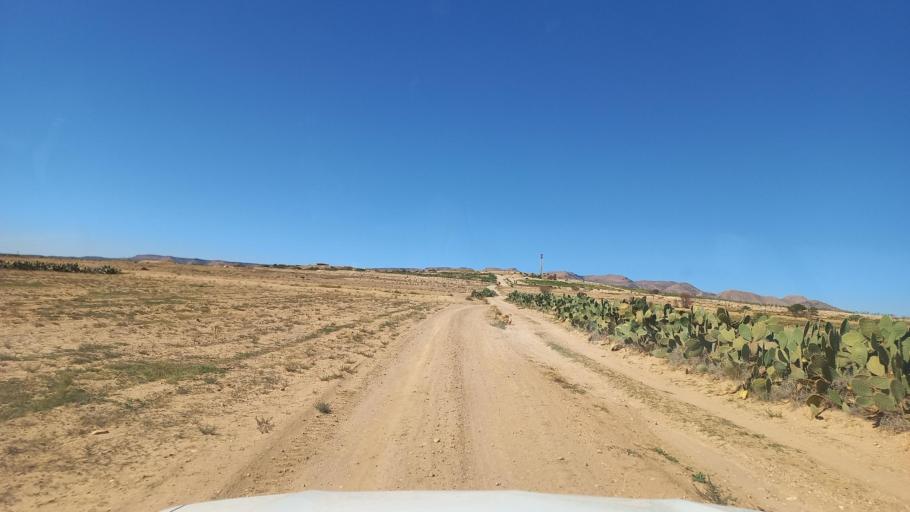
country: TN
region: Al Qasrayn
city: Sbiba
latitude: 35.3725
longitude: 9.0824
